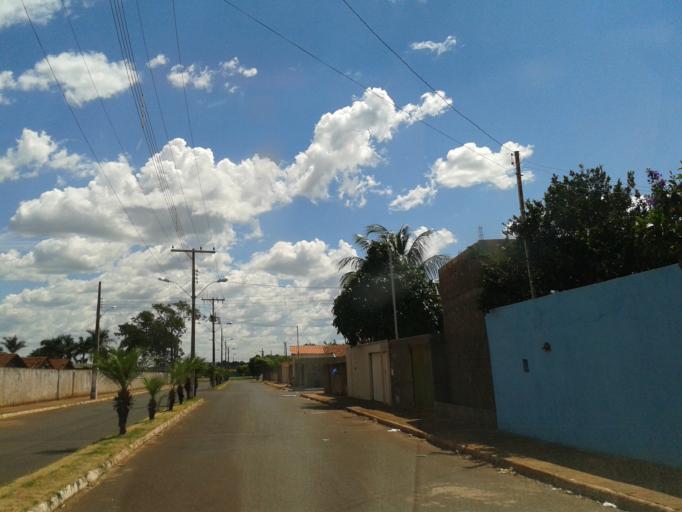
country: BR
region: Minas Gerais
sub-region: Centralina
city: Centralina
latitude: -18.7262
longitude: -49.1943
